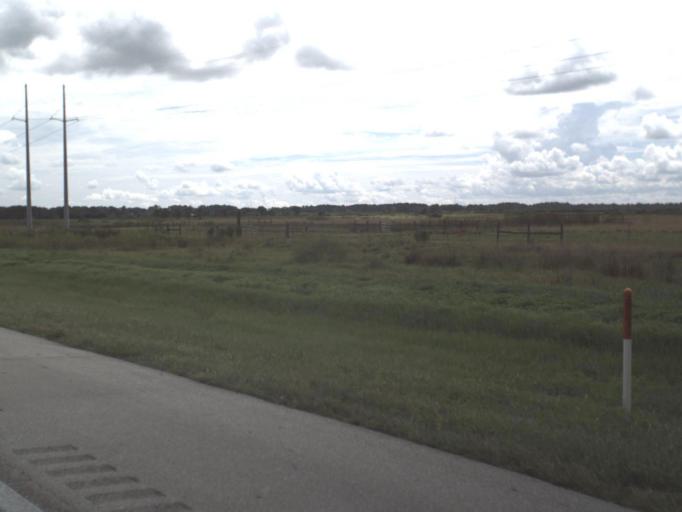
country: US
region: Florida
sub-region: Polk County
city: Polk City
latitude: 28.1478
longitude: -81.8701
